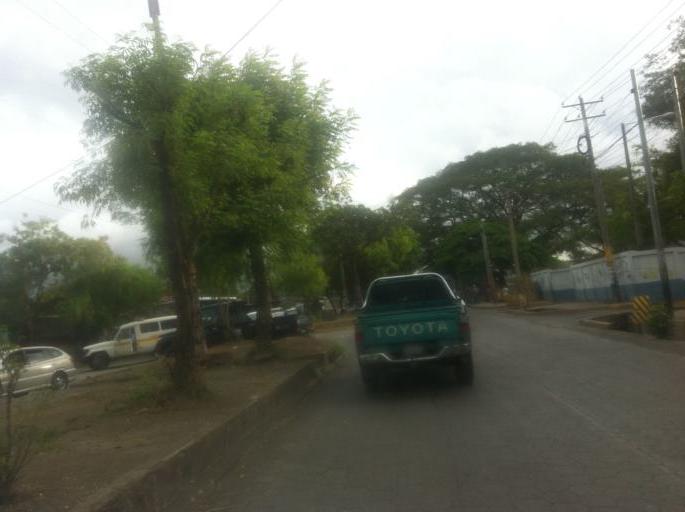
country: NI
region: Managua
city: Managua
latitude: 12.1215
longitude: -86.2450
